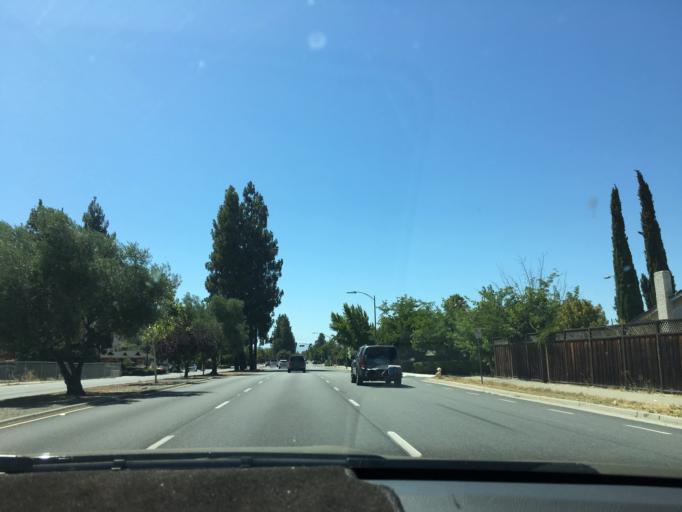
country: US
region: California
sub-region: Santa Clara County
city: Seven Trees
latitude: 37.2372
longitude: -121.8435
